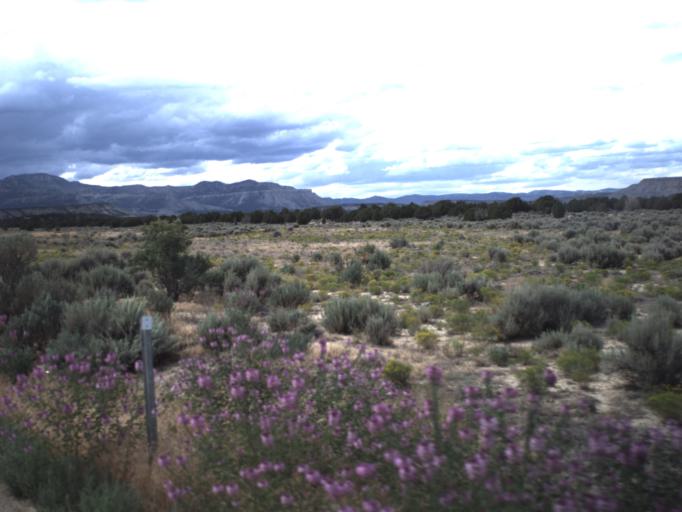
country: US
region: Utah
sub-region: Carbon County
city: Price
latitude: 39.4845
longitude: -110.9020
